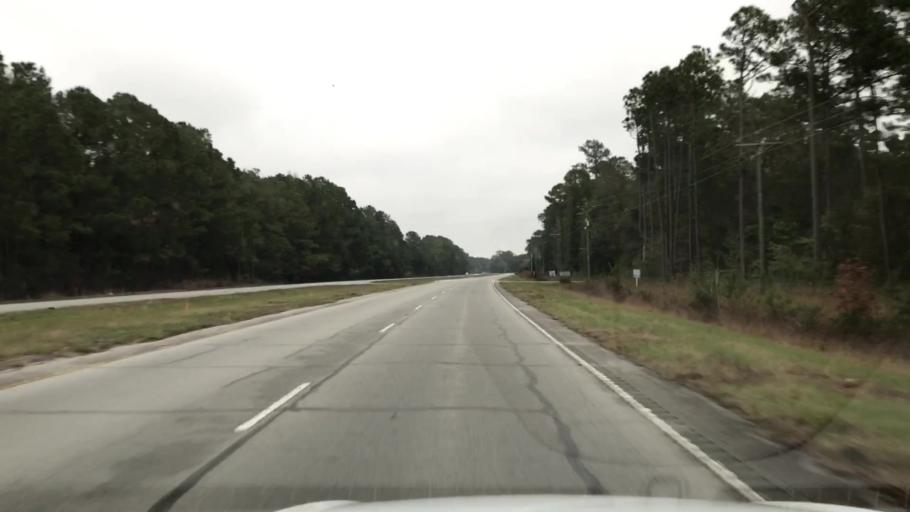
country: US
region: South Carolina
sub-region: Charleston County
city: Awendaw
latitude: 33.0702
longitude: -79.5213
